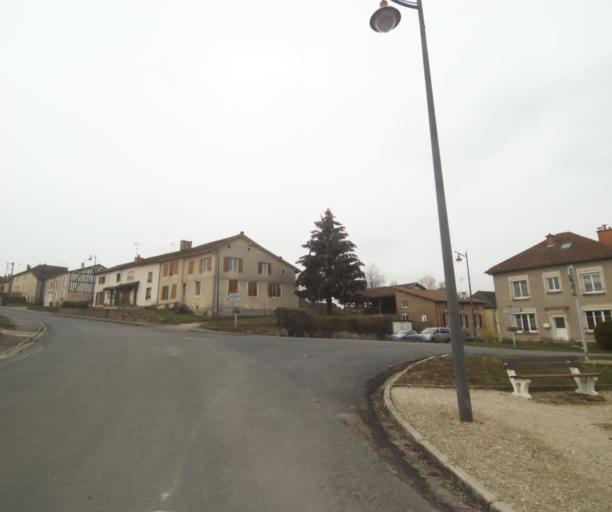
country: FR
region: Champagne-Ardenne
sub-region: Departement de la Marne
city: Sermaize-les-Bains
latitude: 48.7370
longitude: 4.9043
